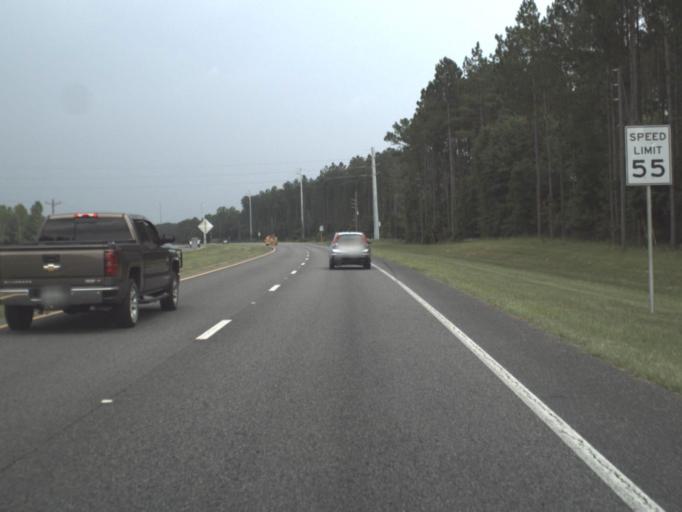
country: US
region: Florida
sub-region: Levy County
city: Chiefland
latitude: 29.4779
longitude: -82.8504
